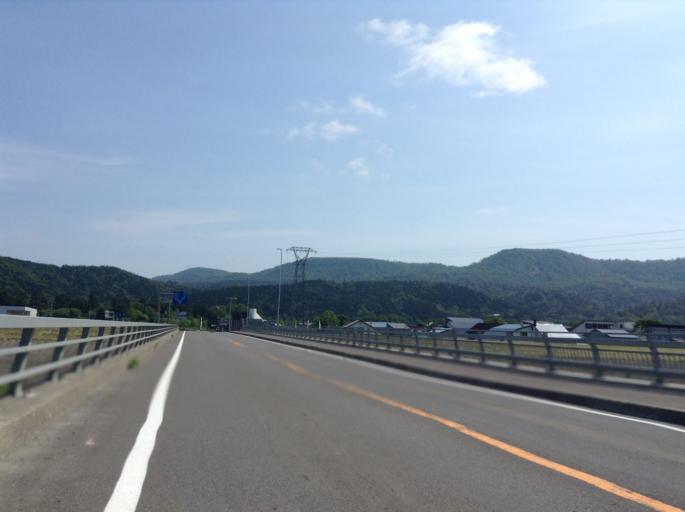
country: JP
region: Hokkaido
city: Nayoro
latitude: 44.7273
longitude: 142.2552
